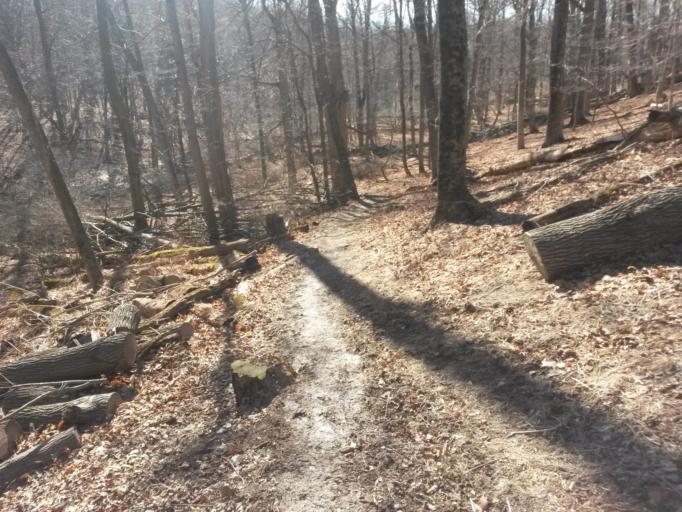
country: US
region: New York
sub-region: Westchester County
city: Yorktown Heights
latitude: 41.2522
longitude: -73.7715
